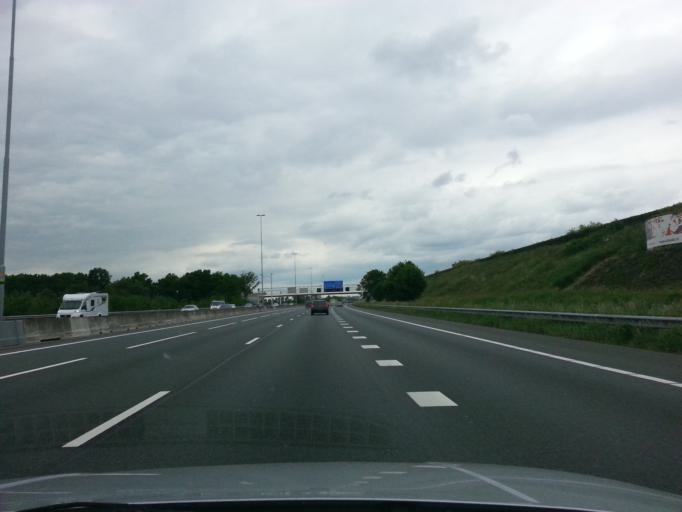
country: NL
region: Gelderland
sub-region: Gemeente Ede
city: Ede
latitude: 52.0175
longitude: 5.6356
